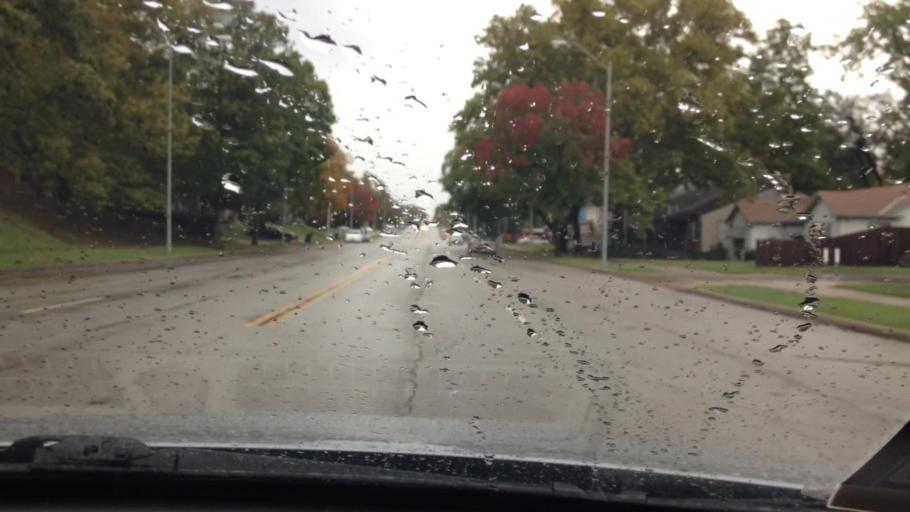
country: US
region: Kansas
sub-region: Johnson County
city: Westwood
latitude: 39.0470
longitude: -94.5680
